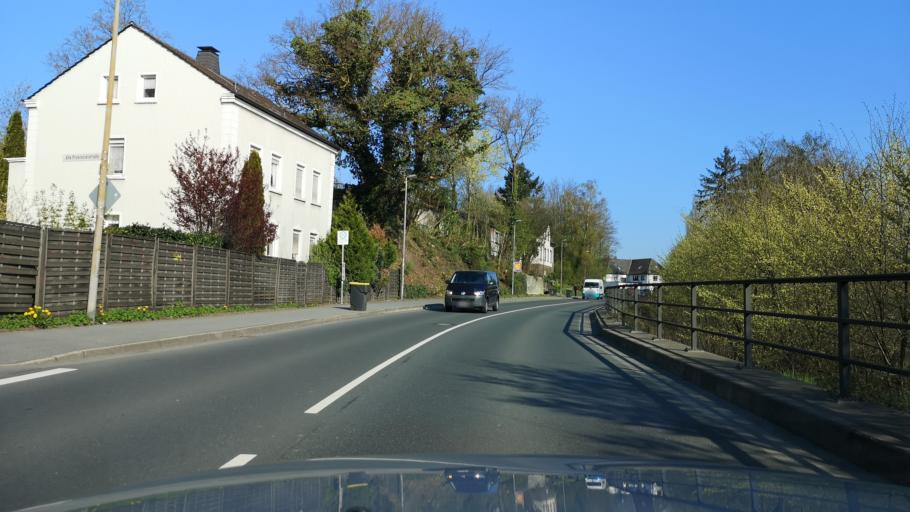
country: DE
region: North Rhine-Westphalia
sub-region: Regierungsbezirk Arnsberg
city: Menden
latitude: 51.4445
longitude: 7.7788
